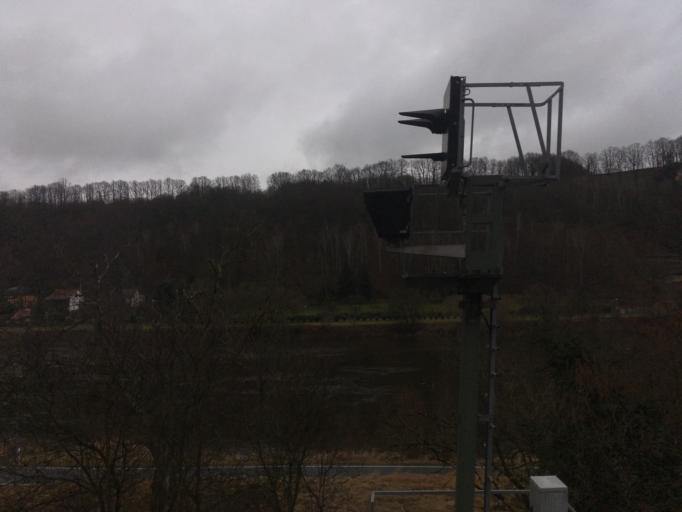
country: DE
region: Saxony
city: Struppen
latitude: 50.9530
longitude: 13.9812
